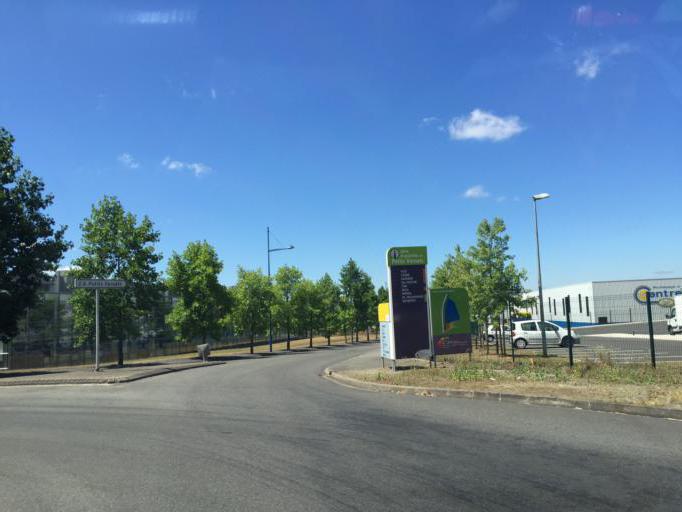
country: FR
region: Auvergne
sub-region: Departement de l'Allier
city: Avermes
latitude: 46.5935
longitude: 3.3313
